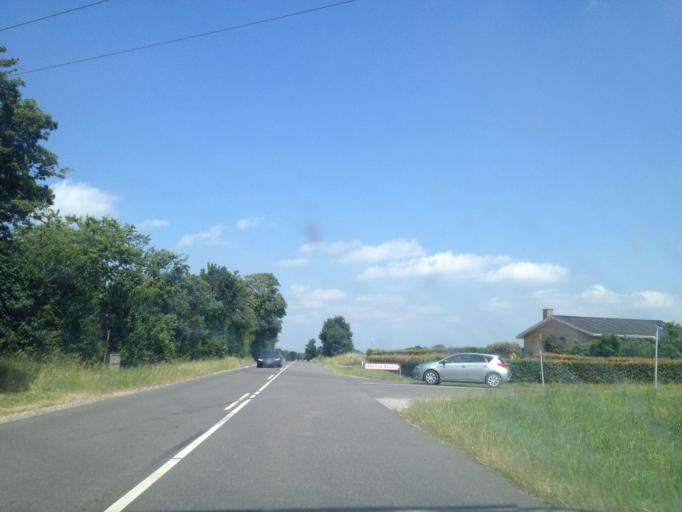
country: DK
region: South Denmark
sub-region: Kolding Kommune
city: Vamdrup
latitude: 55.4109
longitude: 9.2561
